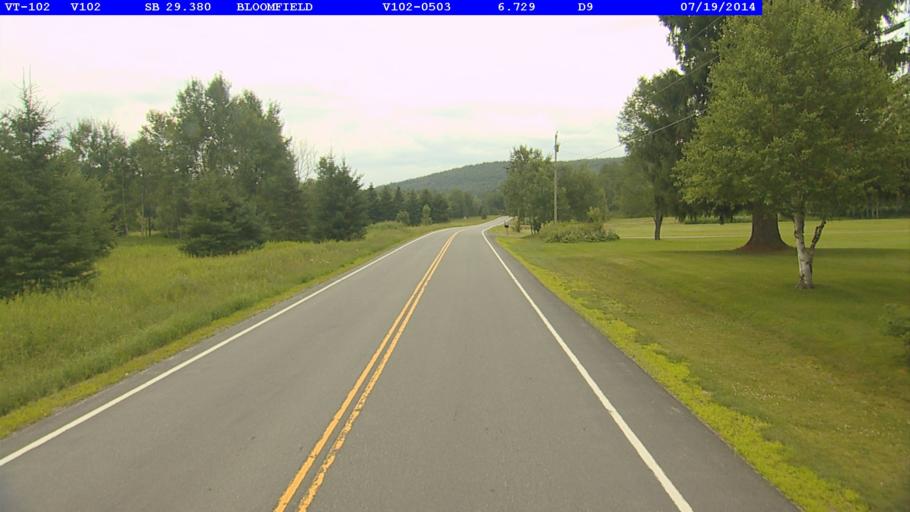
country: US
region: New Hampshire
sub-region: Coos County
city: Colebrook
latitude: 44.8247
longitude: -71.5687
